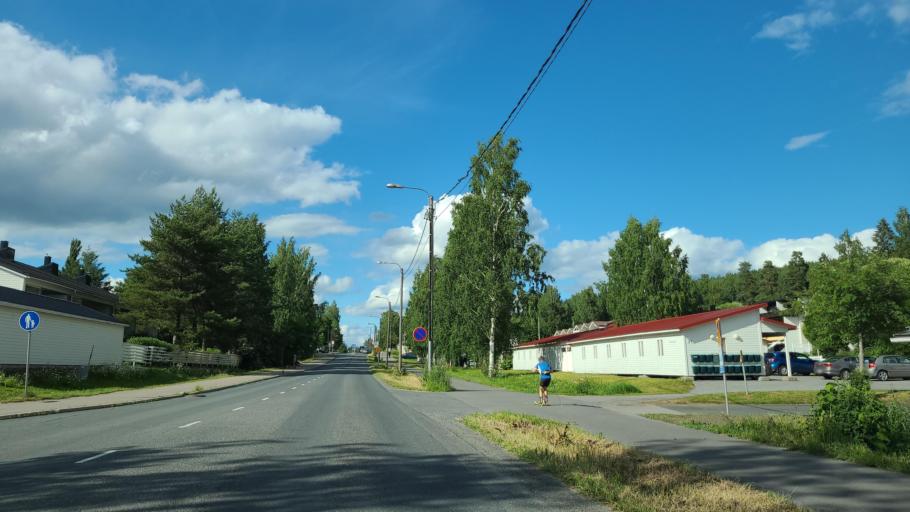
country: FI
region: Northern Savo
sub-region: Kuopio
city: Kuopio
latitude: 62.9234
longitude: 27.6320
